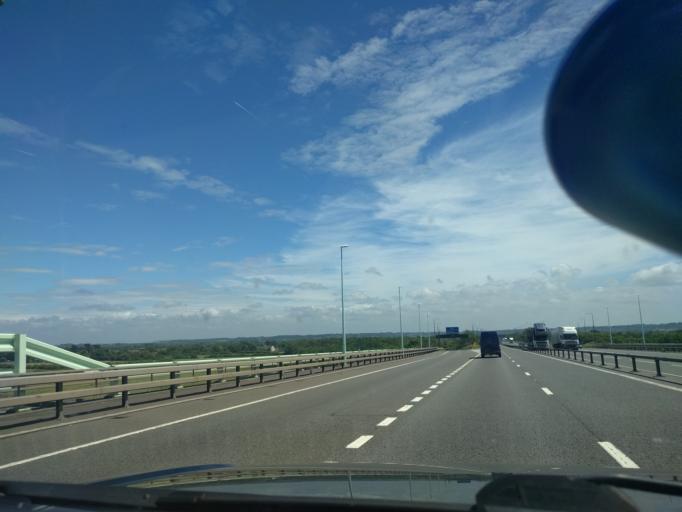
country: GB
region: England
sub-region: South Gloucestershire
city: Severn Beach
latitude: 51.5696
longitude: -2.6662
